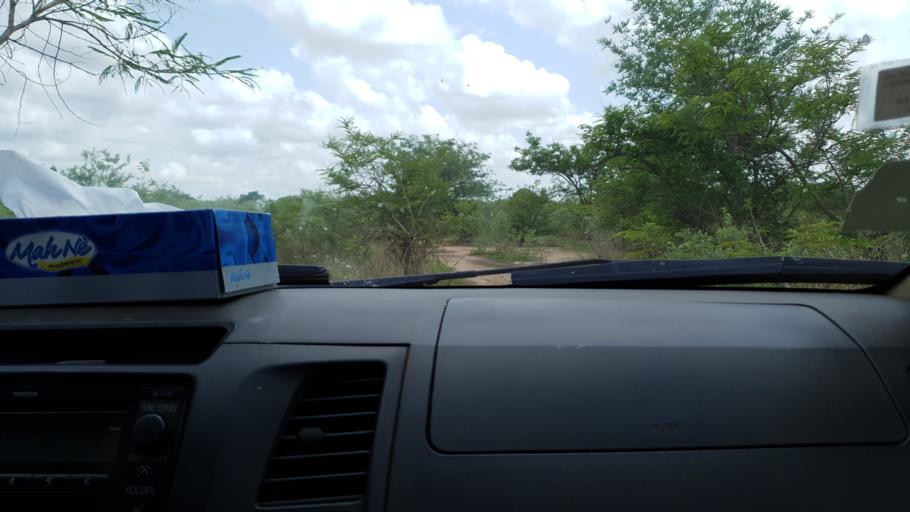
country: ML
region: Segou
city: Baroueli
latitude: 13.3484
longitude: -7.0947
